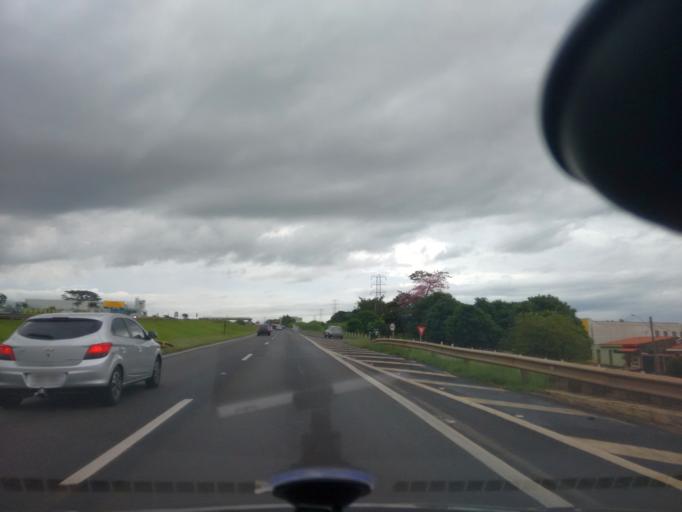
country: BR
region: Sao Paulo
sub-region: Rio Claro
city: Rio Claro
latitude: -22.4189
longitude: -47.5780
